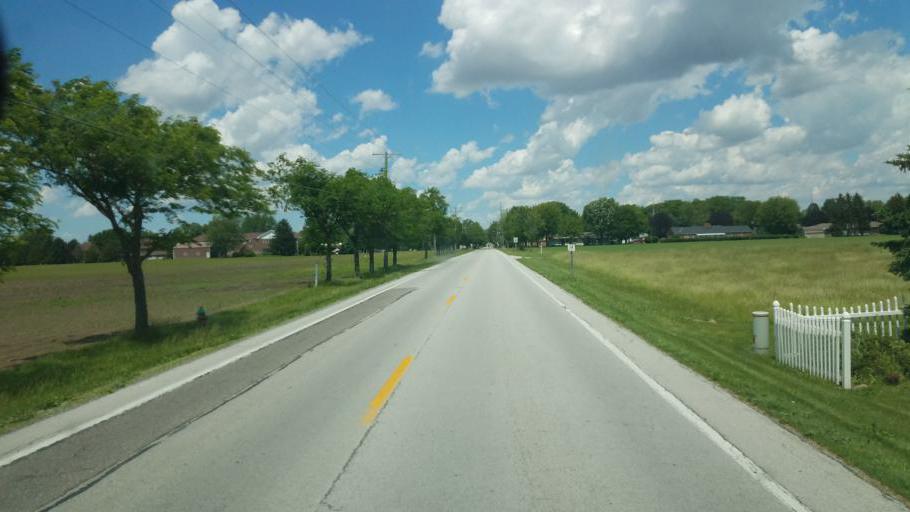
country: US
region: Ohio
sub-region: Wyandot County
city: Upper Sandusky
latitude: 40.8116
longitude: -83.2841
